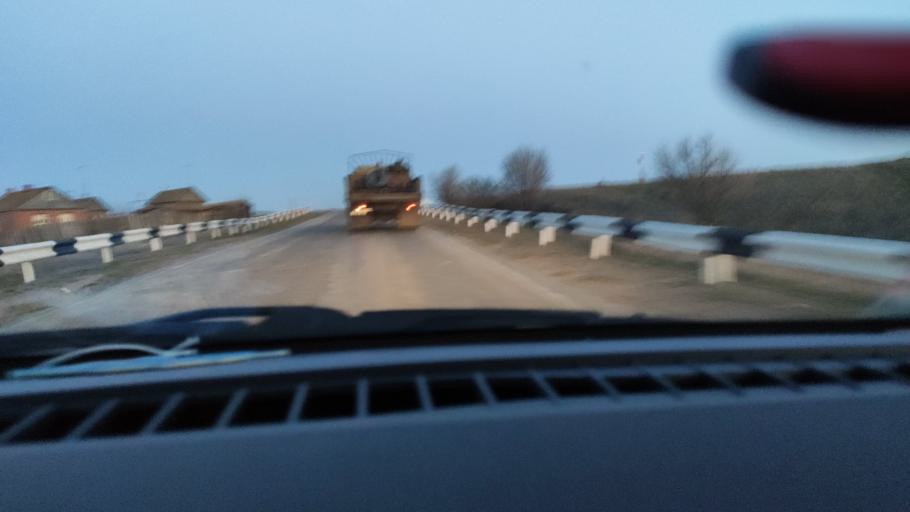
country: RU
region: Saratov
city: Rovnoye
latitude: 51.0270
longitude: 46.0919
